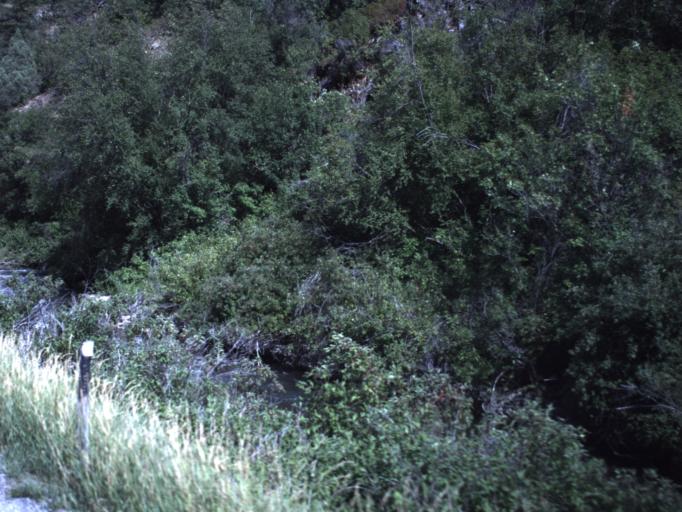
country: US
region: Utah
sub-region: Cache County
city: North Logan
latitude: 41.8078
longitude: -111.6283
